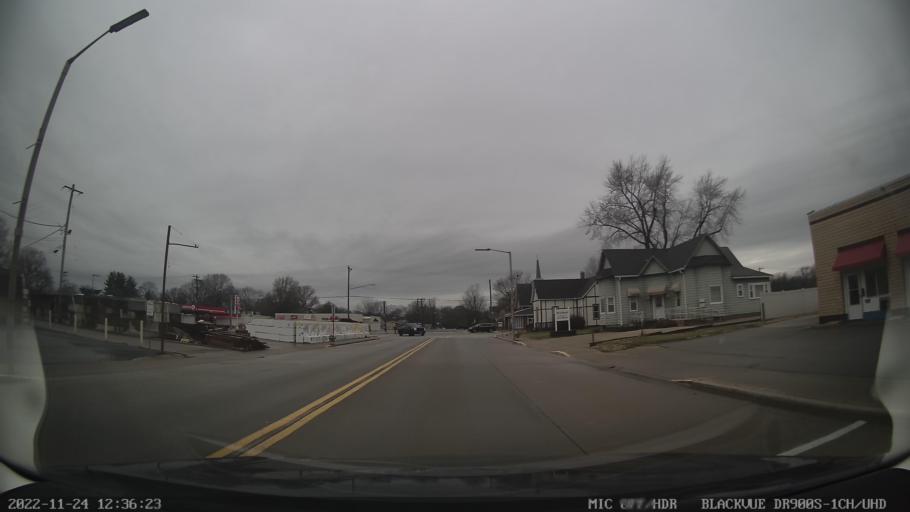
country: US
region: Illinois
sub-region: Macoupin County
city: Staunton
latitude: 39.0121
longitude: -89.7903
